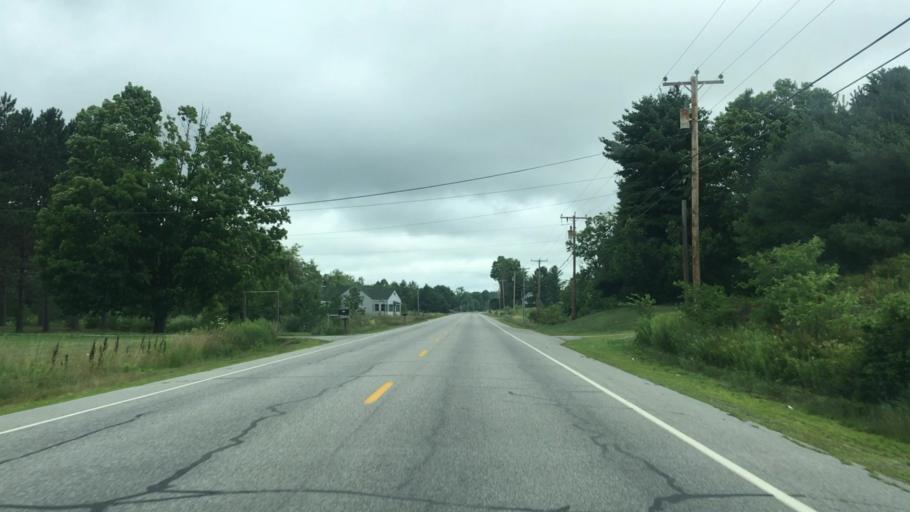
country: US
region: Maine
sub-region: Kennebec County
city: Pittston
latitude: 44.1532
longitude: -69.7442
